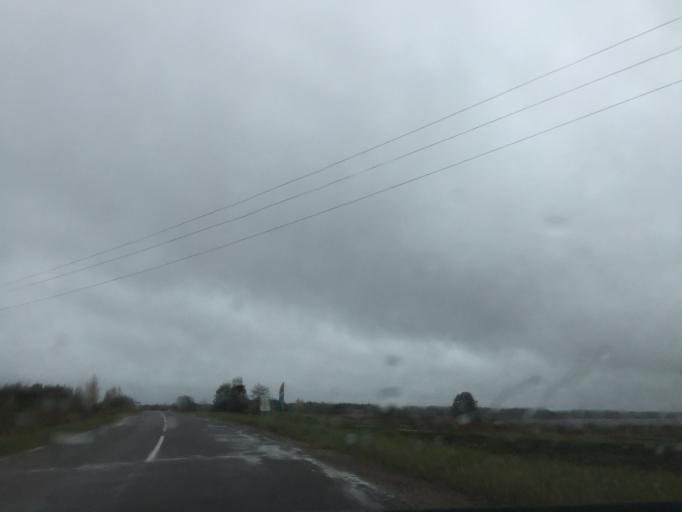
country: LV
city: Tireli
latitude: 56.8095
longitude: 23.5827
